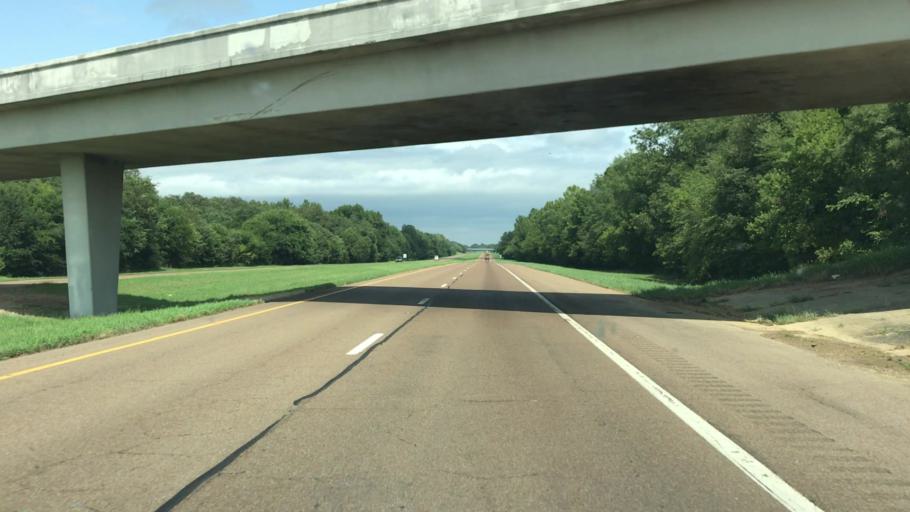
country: US
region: Tennessee
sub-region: Obion County
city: South Fulton
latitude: 36.4821
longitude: -88.9412
